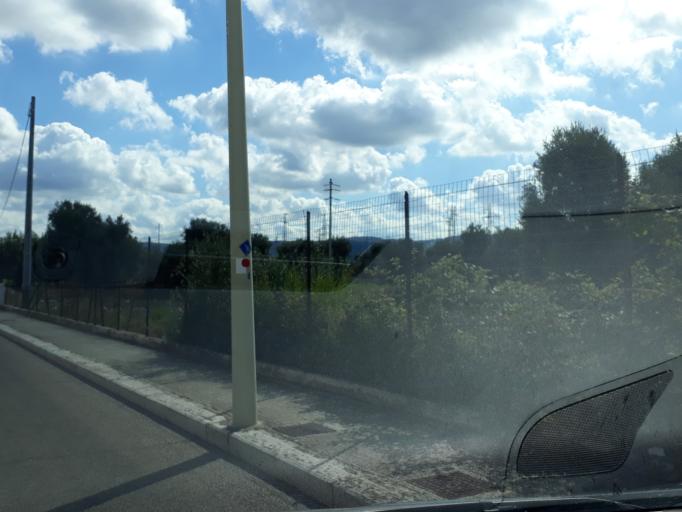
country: IT
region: Apulia
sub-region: Provincia di Brindisi
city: Fasano
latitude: 40.8269
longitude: 17.3617
